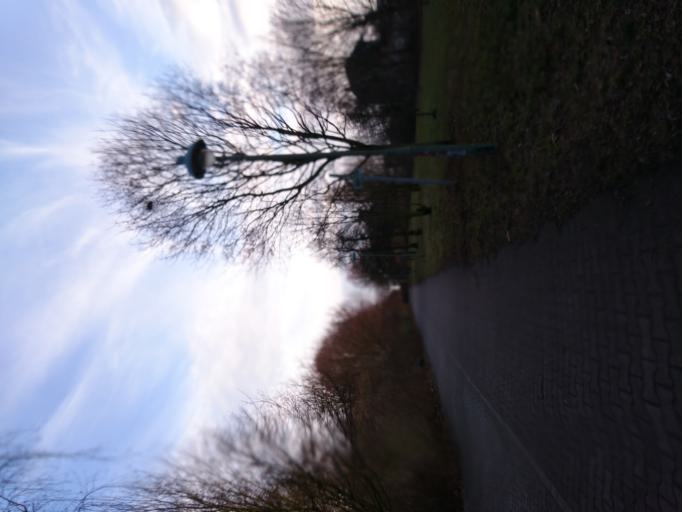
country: DE
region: Berlin
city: Tegel
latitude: 52.5882
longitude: 13.2904
